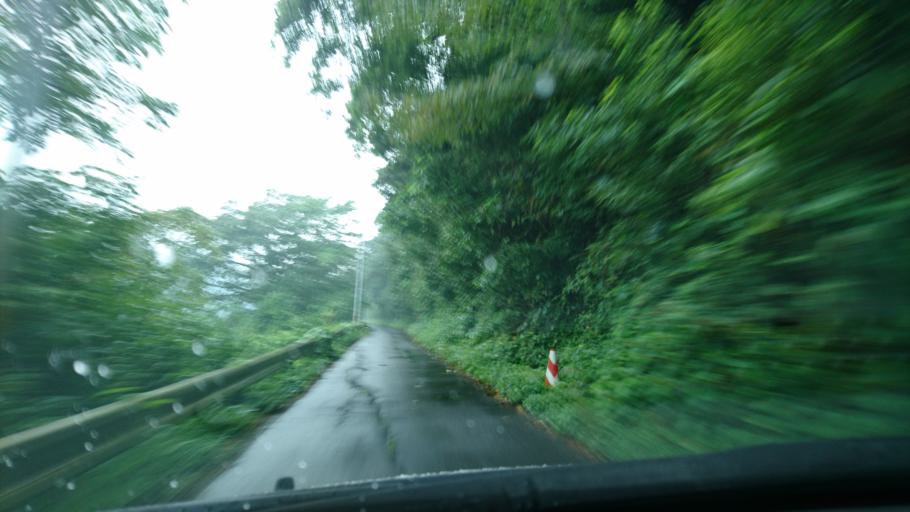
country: JP
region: Iwate
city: Ichinoseki
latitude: 38.8764
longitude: 141.2592
